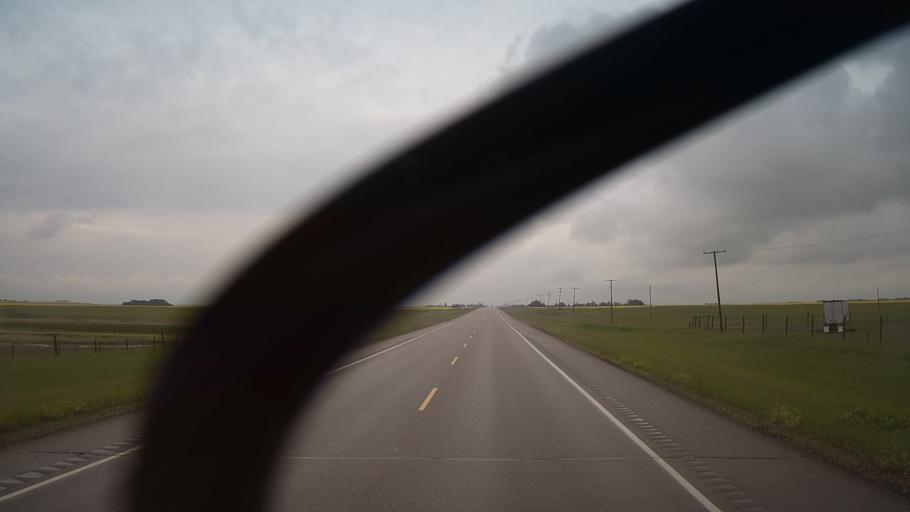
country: CA
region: Saskatchewan
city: Unity
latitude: 52.4350
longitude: -109.0000
